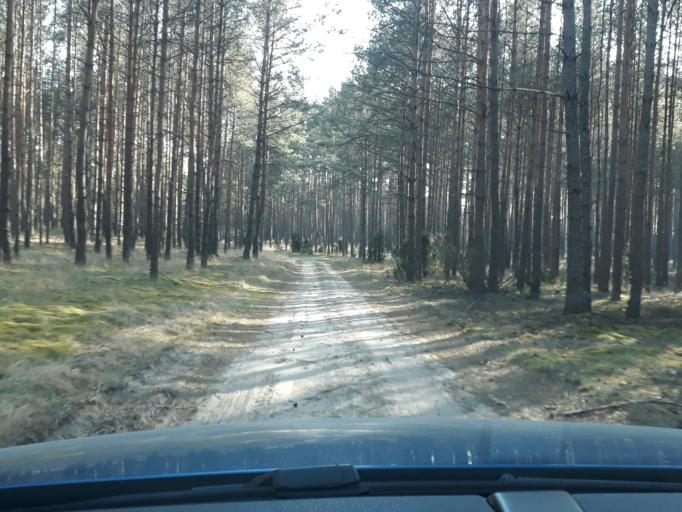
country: PL
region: Pomeranian Voivodeship
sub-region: Powiat bytowski
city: Lipnica
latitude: 53.9061
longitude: 17.4957
